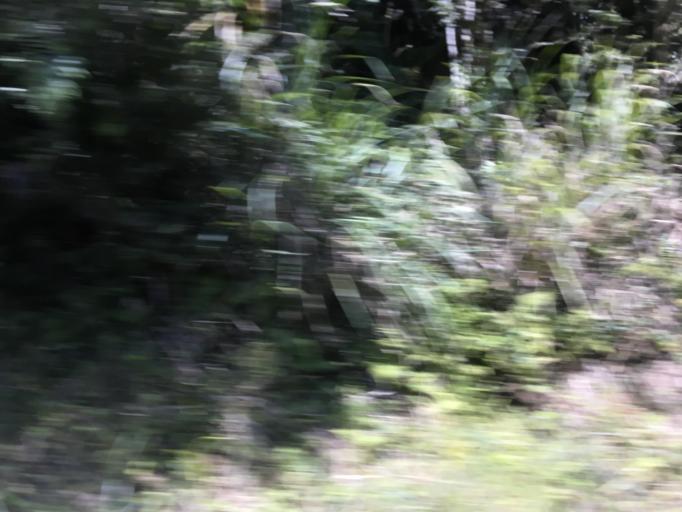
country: TW
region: Taiwan
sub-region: Yilan
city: Yilan
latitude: 24.5204
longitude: 121.5213
